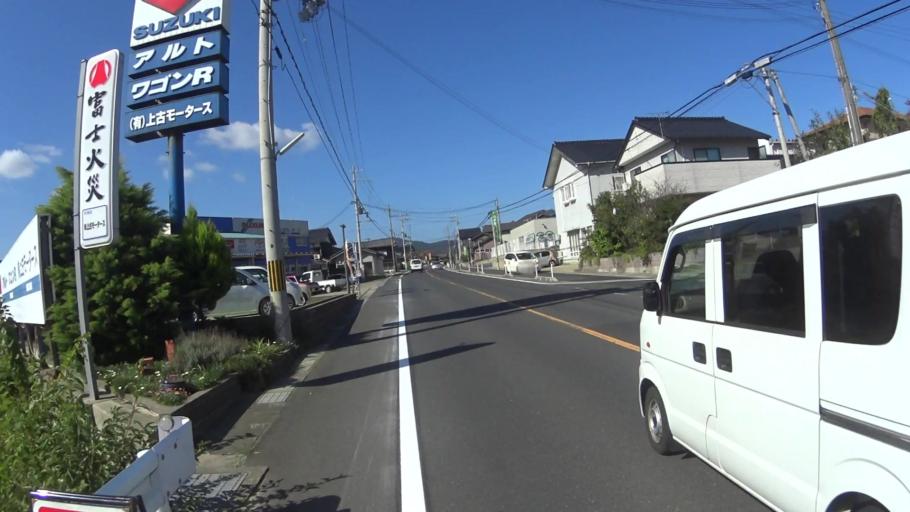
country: JP
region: Kyoto
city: Miyazu
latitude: 35.6822
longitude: 135.0395
